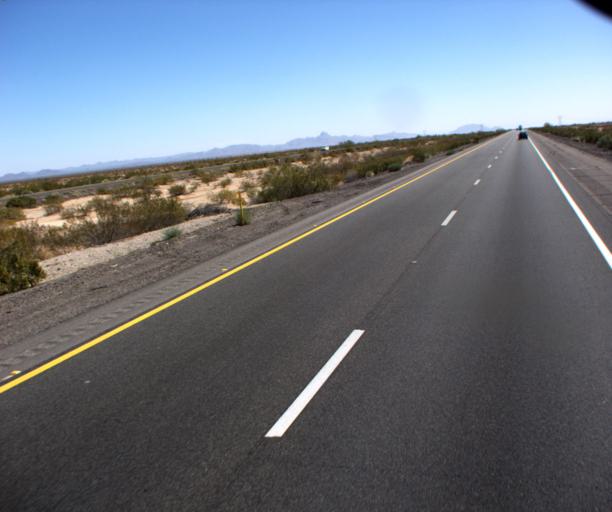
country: US
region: Arizona
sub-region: La Paz County
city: Salome
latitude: 33.5799
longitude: -113.4270
